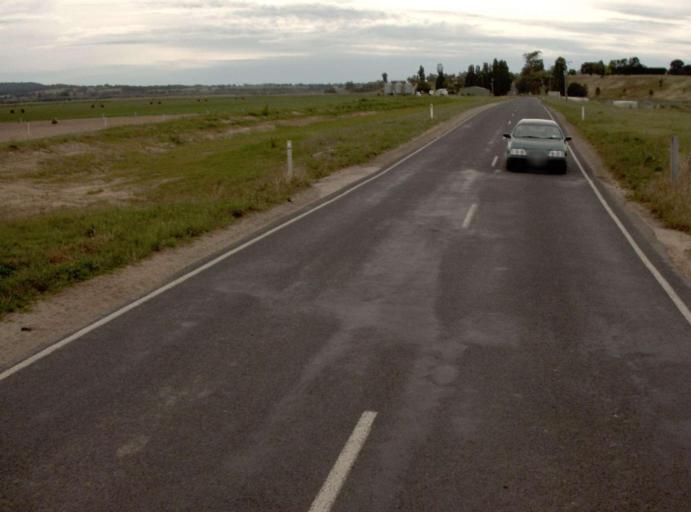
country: AU
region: Victoria
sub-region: East Gippsland
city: Bairnsdale
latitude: -37.7986
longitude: 147.4434
